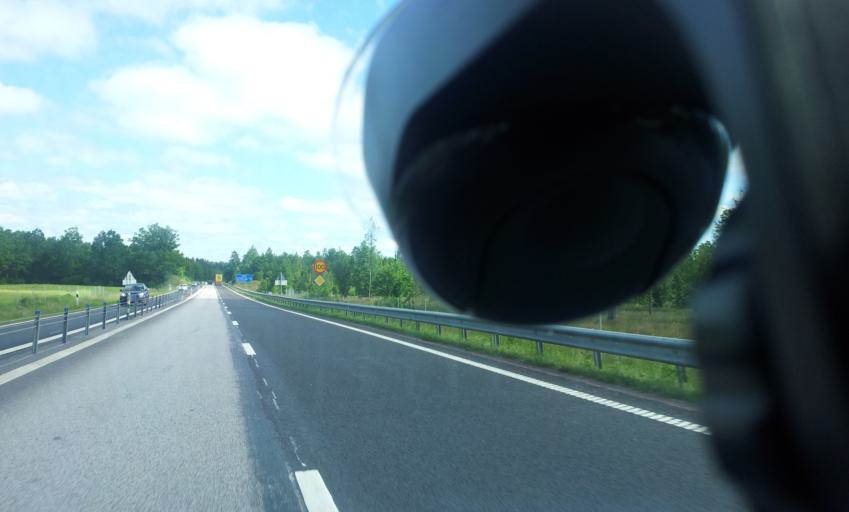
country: SE
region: Kalmar
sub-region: Monsteras Kommun
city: Timmernabben
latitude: 56.8524
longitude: 16.3784
